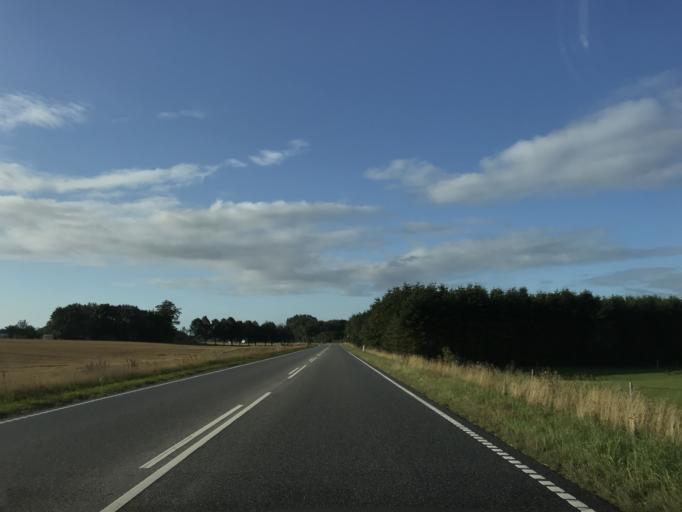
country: DK
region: Central Jutland
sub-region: Skanderborg Kommune
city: Skanderborg
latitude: 56.0727
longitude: 9.8960
